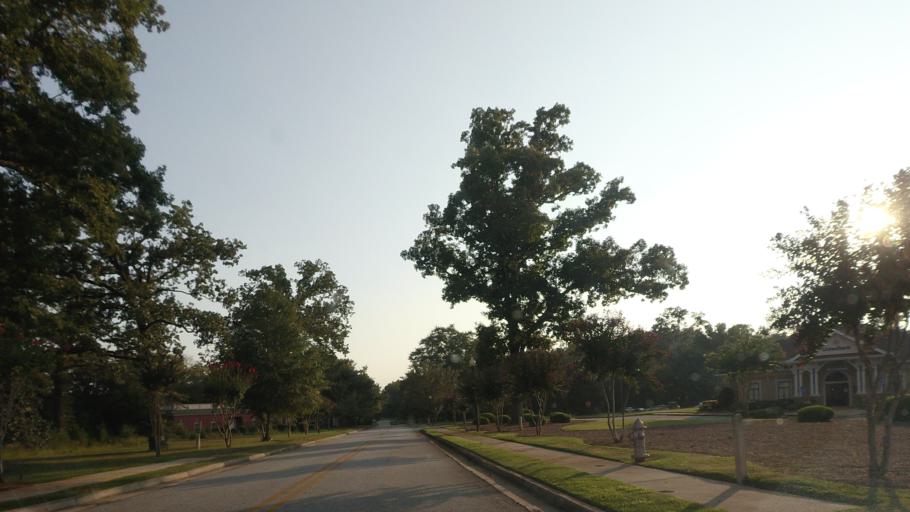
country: US
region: Georgia
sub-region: Monroe County
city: Forsyth
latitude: 32.9509
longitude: -83.8055
